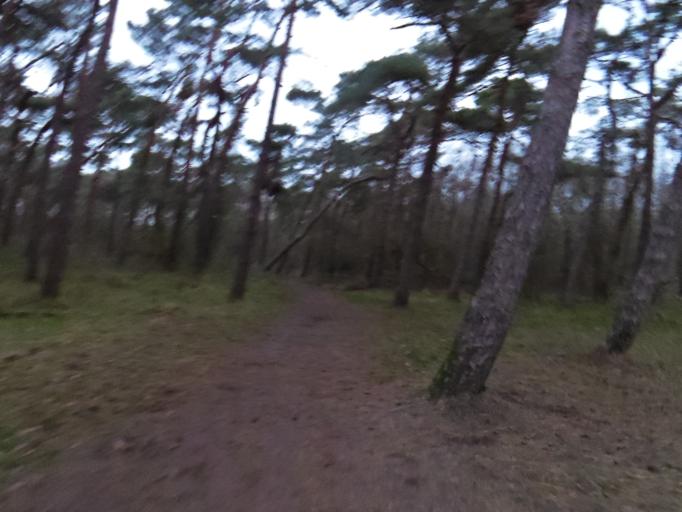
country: NL
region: North Holland
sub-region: Gemeente Zandvoort
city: Zandvoort
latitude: 52.3579
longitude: 4.5740
